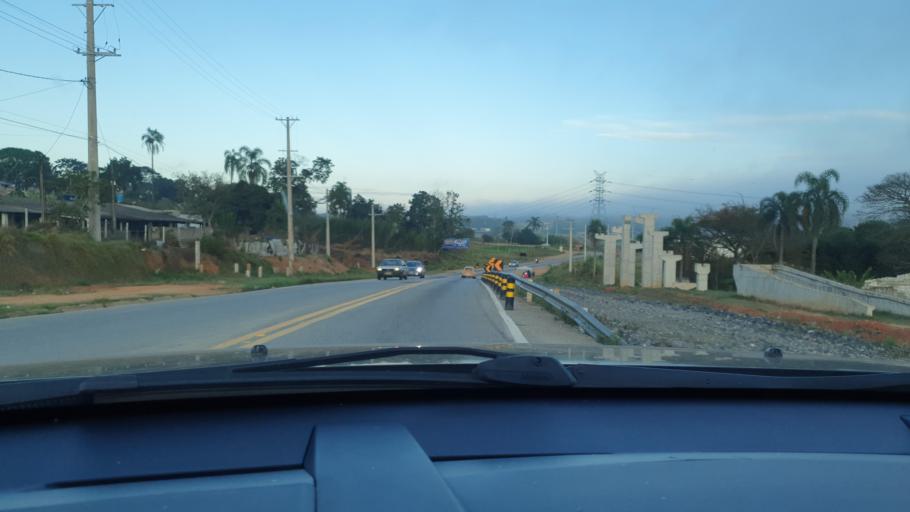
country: BR
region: Sao Paulo
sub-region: Vargem Grande Paulista
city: Vargem Grande Paulista
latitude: -23.6564
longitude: -47.0776
